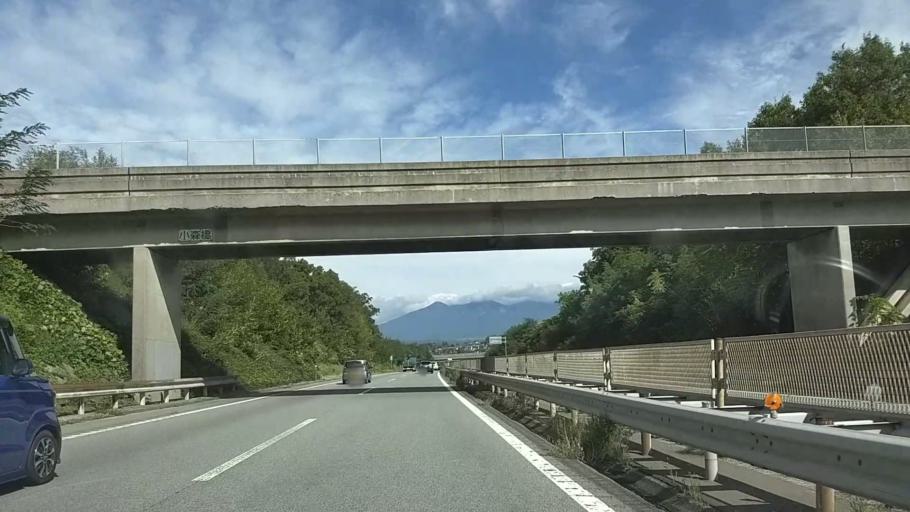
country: JP
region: Yamanashi
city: Nirasaki
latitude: 35.7471
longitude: 138.4438
